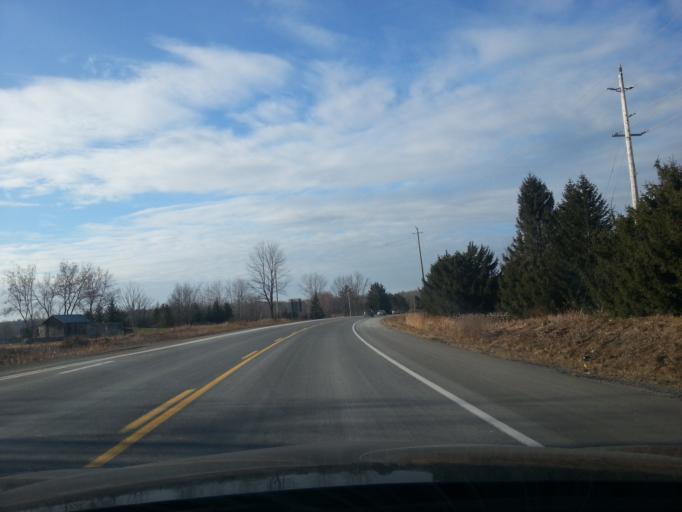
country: CA
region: Ontario
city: Quinte West
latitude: 44.5050
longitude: -77.4954
